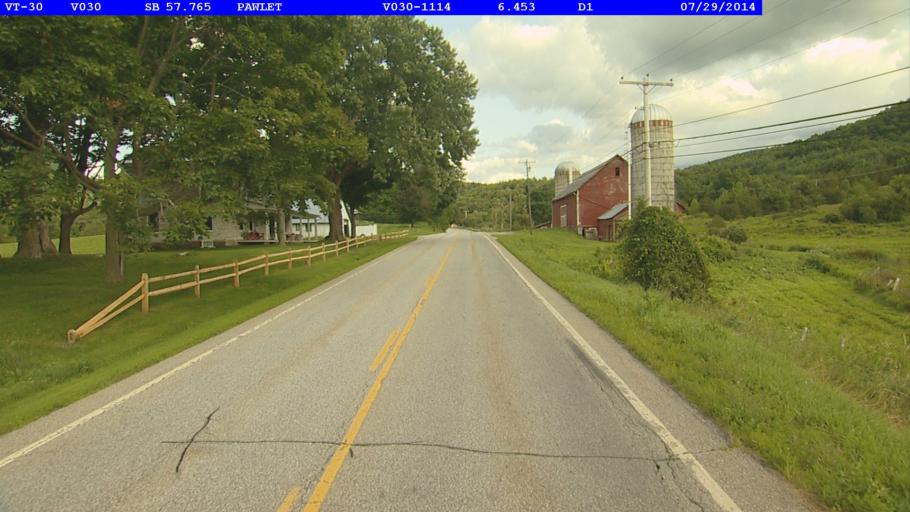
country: US
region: New York
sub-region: Washington County
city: Granville
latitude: 43.3850
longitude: -73.2138
